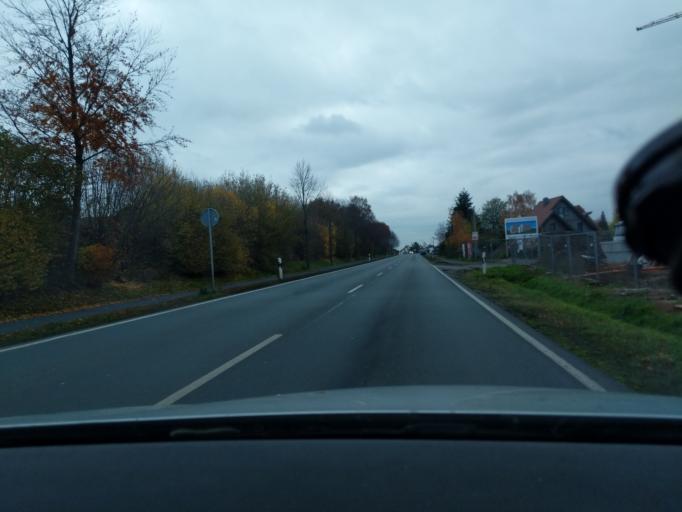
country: DE
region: North Rhine-Westphalia
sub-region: Regierungsbezirk Munster
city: Birgte
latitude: 52.2646
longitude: 7.6180
